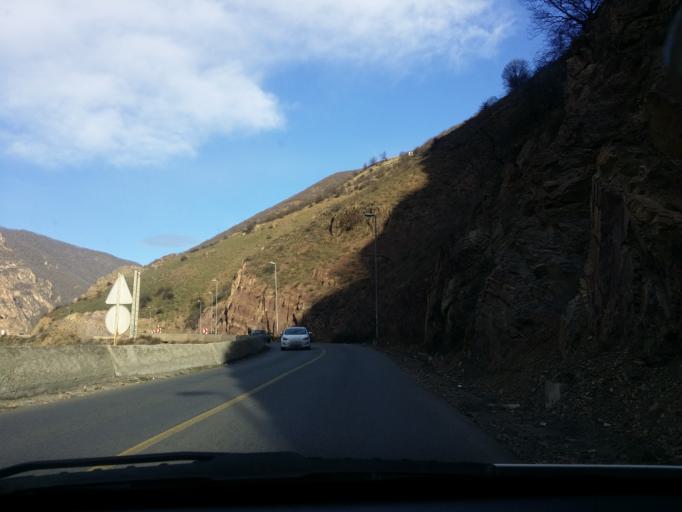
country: IR
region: Mazandaran
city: Chalus
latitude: 36.2646
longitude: 51.2628
